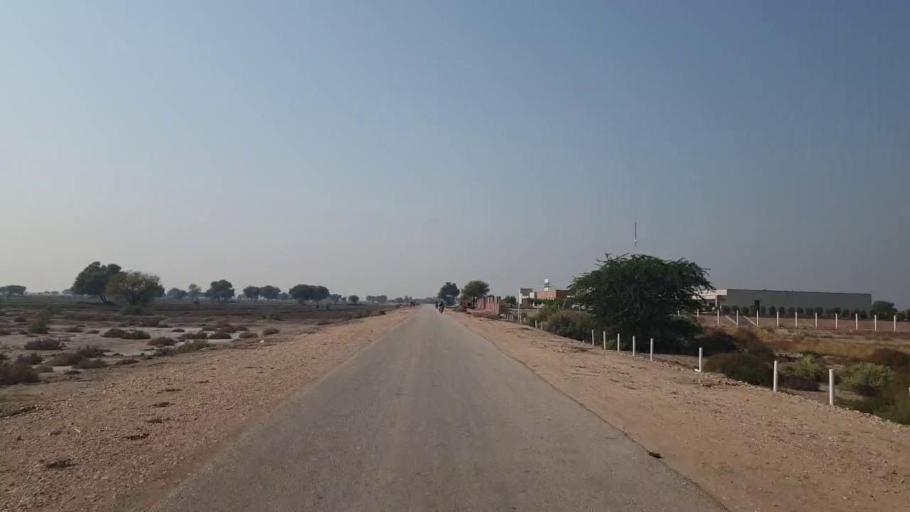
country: PK
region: Sindh
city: Sehwan
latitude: 26.4283
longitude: 67.8371
